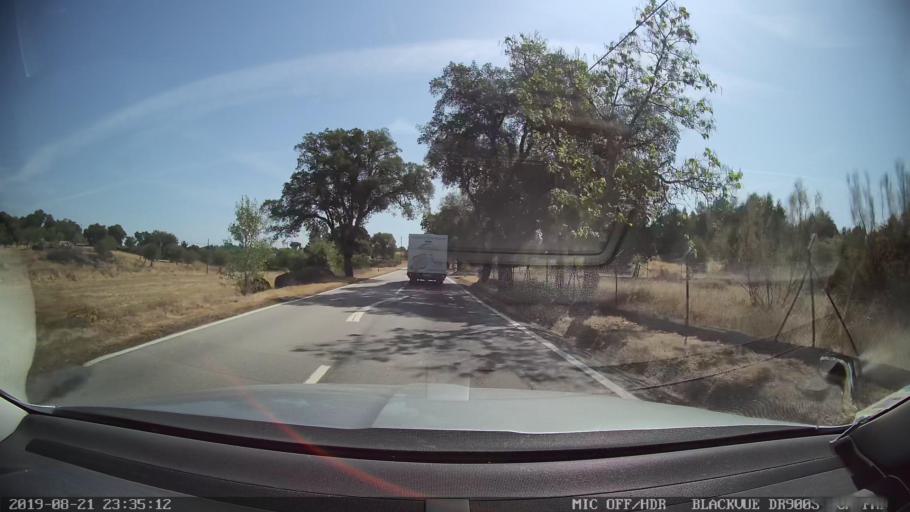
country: PT
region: Guarda
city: Alcains
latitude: 39.8788
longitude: -7.3908
